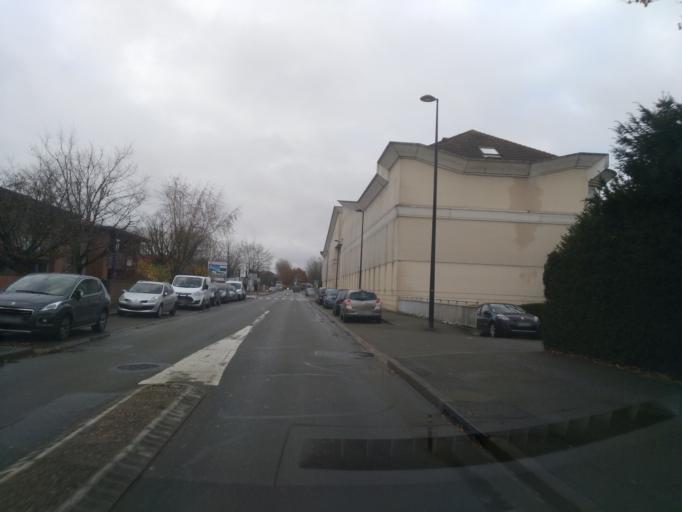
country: FR
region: Ile-de-France
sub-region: Departement des Yvelines
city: Voisins-le-Bretonneux
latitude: 48.7663
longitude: 2.0570
